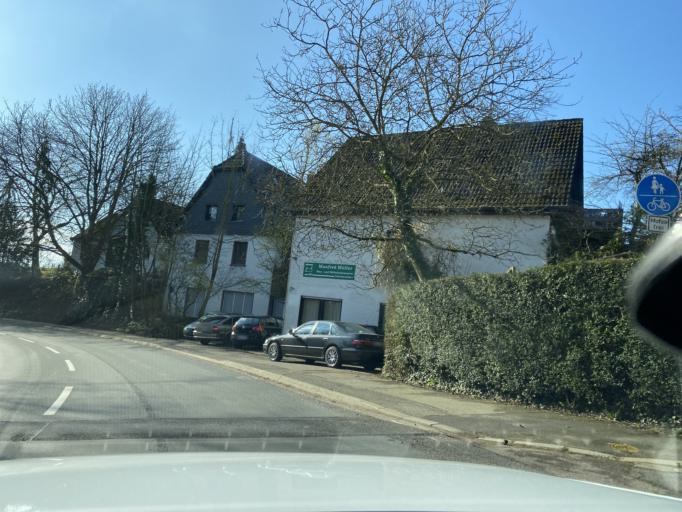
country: DE
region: North Rhine-Westphalia
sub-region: Regierungsbezirk Koln
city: Odenthal
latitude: 51.0590
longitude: 7.1237
